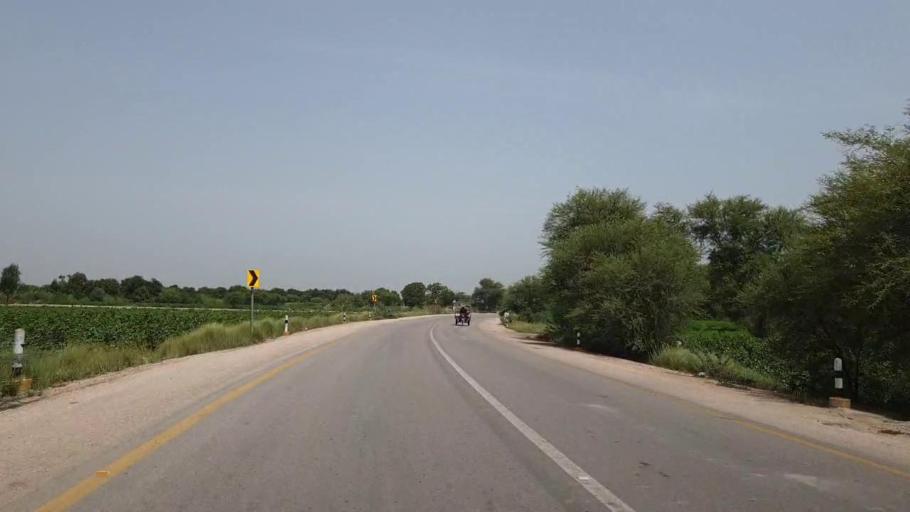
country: PK
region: Sindh
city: Shahpur Chakar
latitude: 26.1493
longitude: 68.6370
